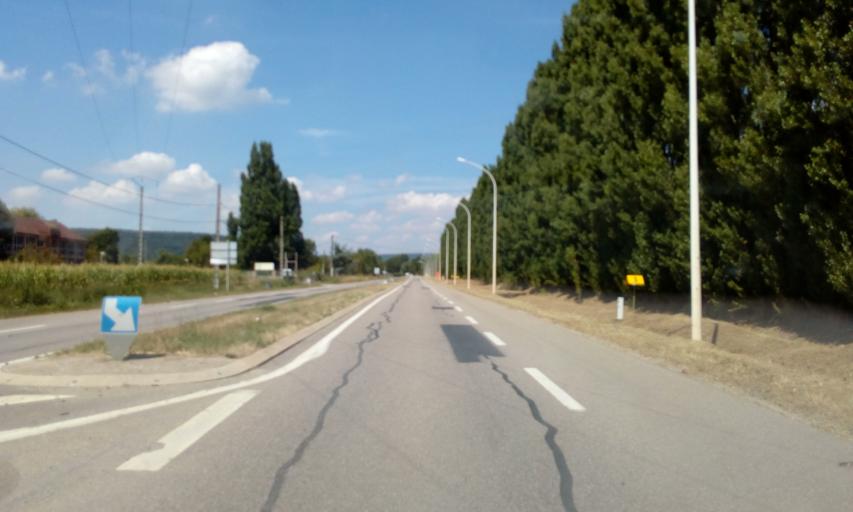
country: FR
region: Lorraine
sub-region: Departement de Meurthe-et-Moselle
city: Blenod-les-Pont-a-Mousson
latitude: 48.8715
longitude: 6.0648
